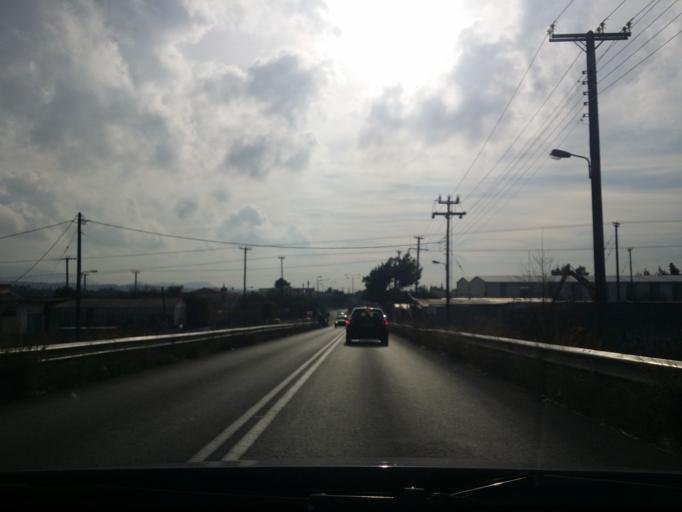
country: GR
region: Attica
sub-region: Nomarchia Athinas
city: Lykovrysi
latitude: 38.0973
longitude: 23.7776
